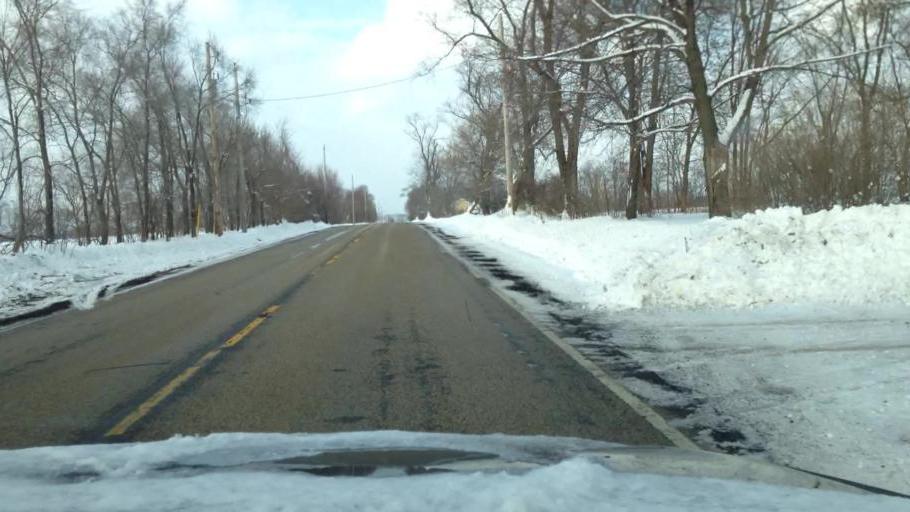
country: US
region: Wisconsin
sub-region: Walworth County
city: East Troy
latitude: 42.7832
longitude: -88.4450
